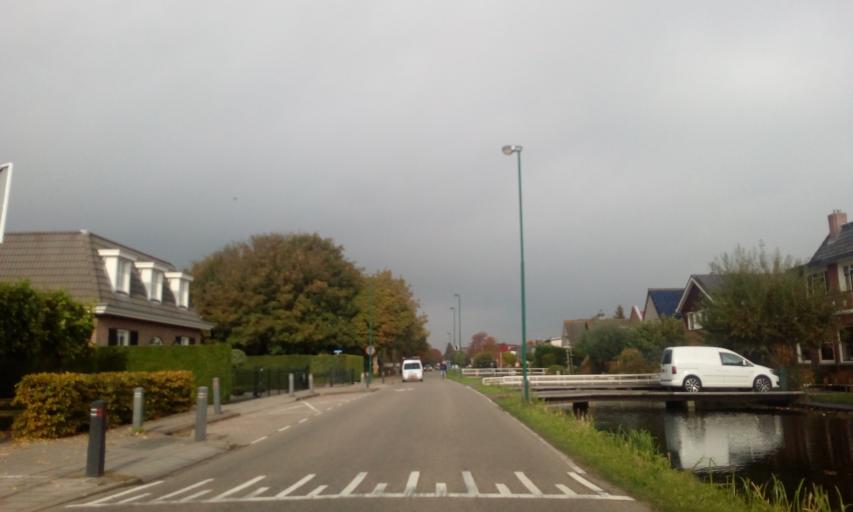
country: NL
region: South Holland
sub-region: Gemeente Lansingerland
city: Bergschenhoek
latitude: 51.9834
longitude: 4.4988
